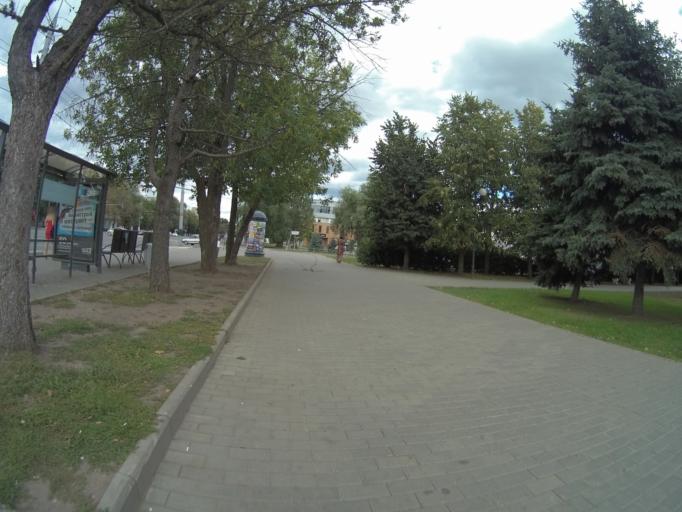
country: RU
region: Vladimir
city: Vladimir
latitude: 56.1193
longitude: 40.3643
